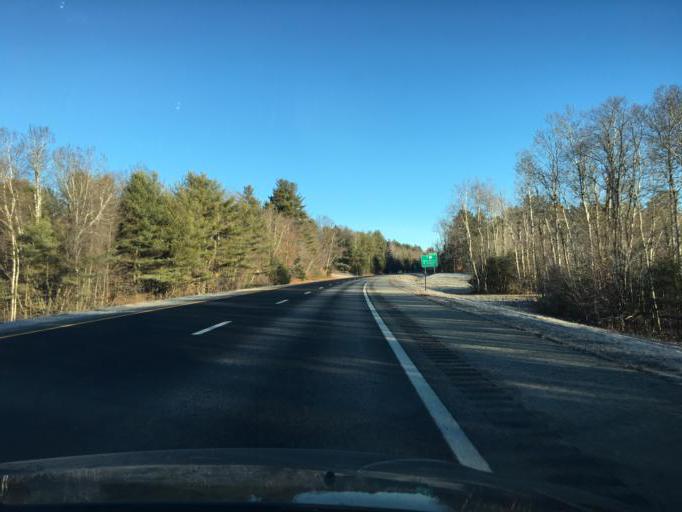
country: US
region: New Hampshire
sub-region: Grafton County
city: Plymouth
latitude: 43.7996
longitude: -71.6766
